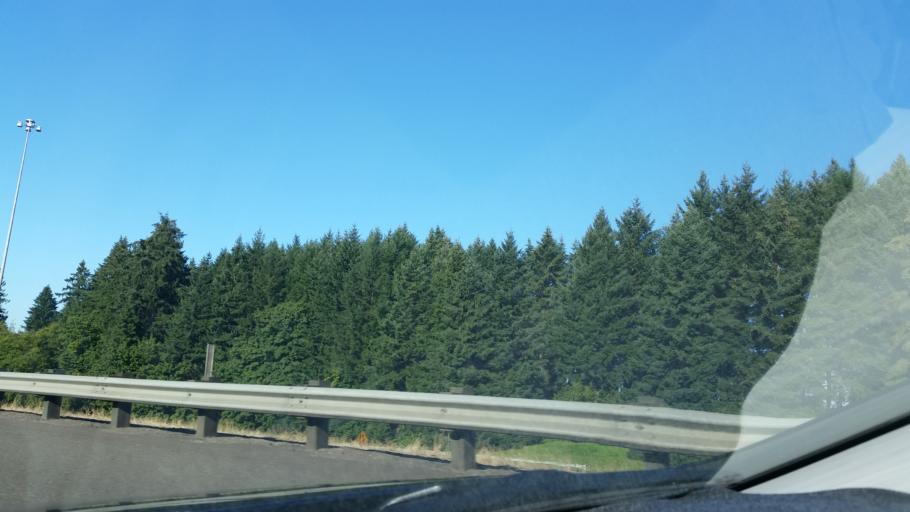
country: US
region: Oregon
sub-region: Clackamas County
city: Wilsonville
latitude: 45.2802
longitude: -122.7695
